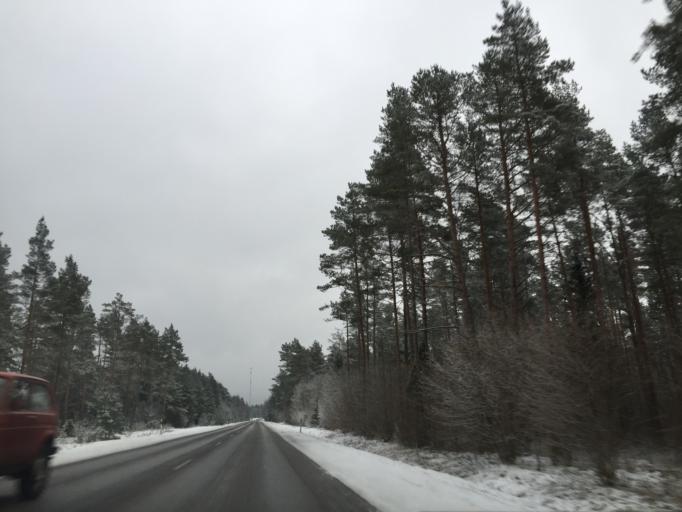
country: EE
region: Laeaene
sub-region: Lihula vald
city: Lihula
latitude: 58.6093
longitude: 23.9437
